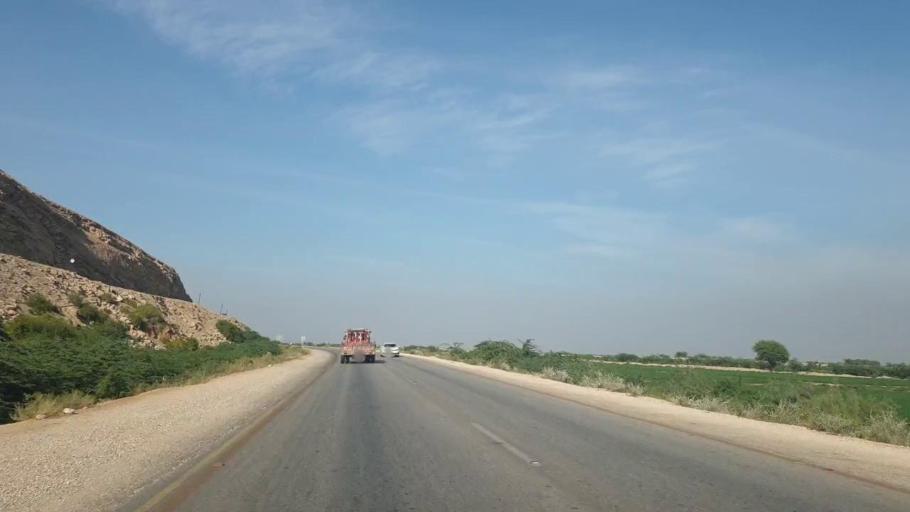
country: PK
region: Sindh
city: Sehwan
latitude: 26.3611
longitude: 67.8736
